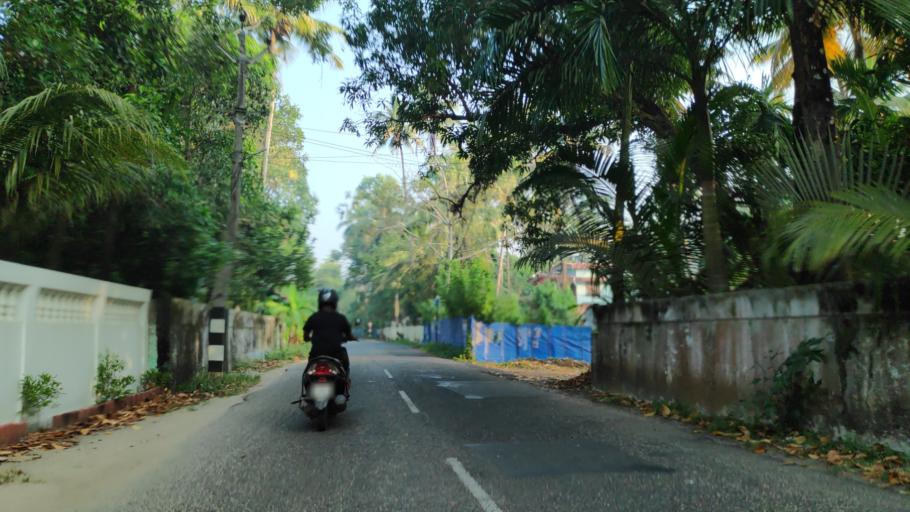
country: IN
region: Kerala
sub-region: Alappuzha
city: Vayalar
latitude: 9.6997
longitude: 76.2897
